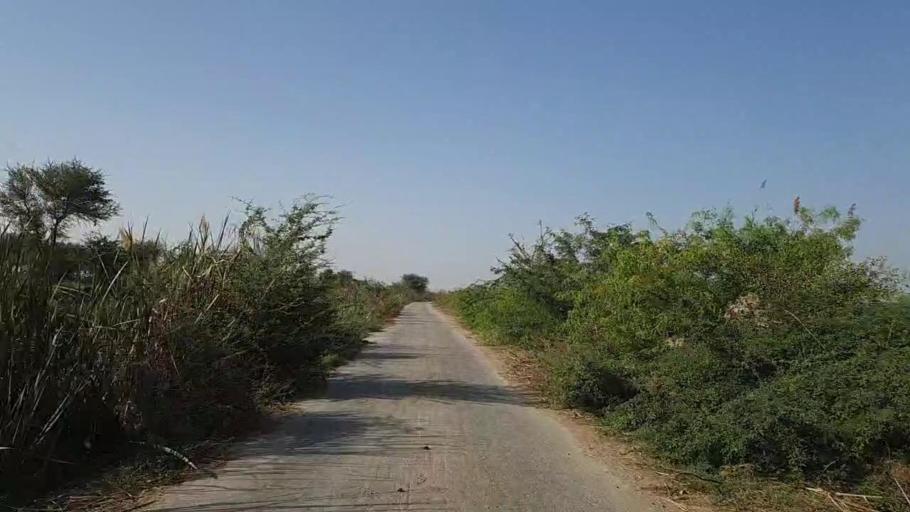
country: PK
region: Sindh
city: Kotri
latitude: 25.1559
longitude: 68.2643
